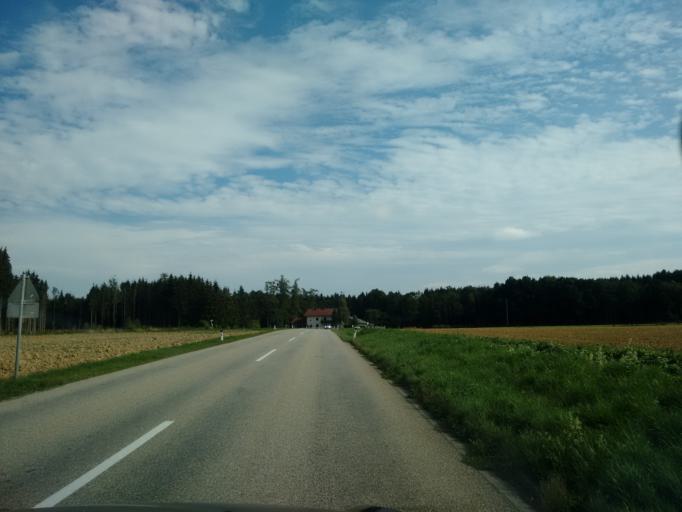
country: AT
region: Upper Austria
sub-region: Wels-Land
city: Thalheim bei Wels
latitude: 48.1383
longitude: 14.0554
